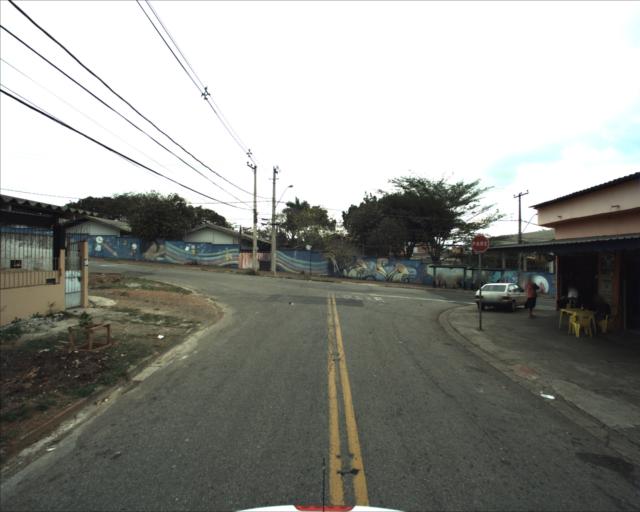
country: BR
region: Sao Paulo
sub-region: Sorocaba
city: Sorocaba
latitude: -23.4328
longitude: -47.5109
